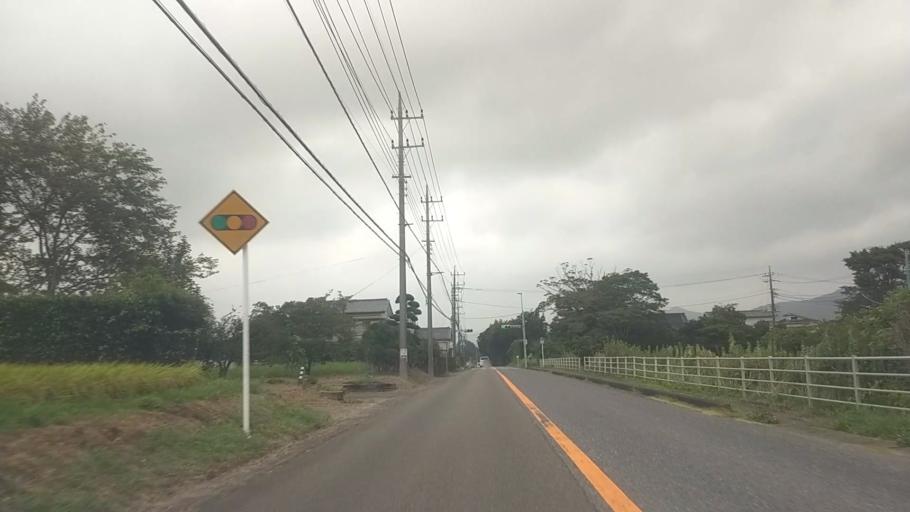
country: JP
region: Chiba
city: Kawaguchi
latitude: 35.1163
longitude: 140.0774
